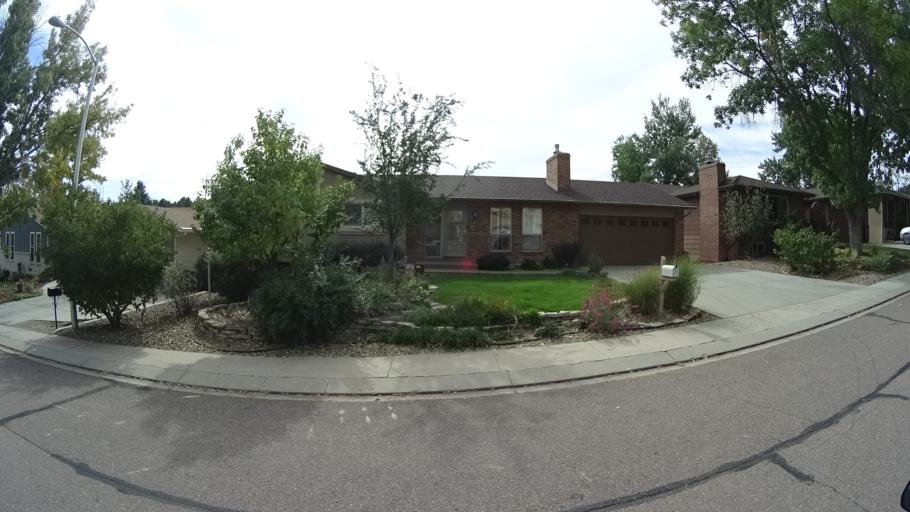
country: US
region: Colorado
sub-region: El Paso County
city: Colorado Springs
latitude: 38.9018
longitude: -104.7834
